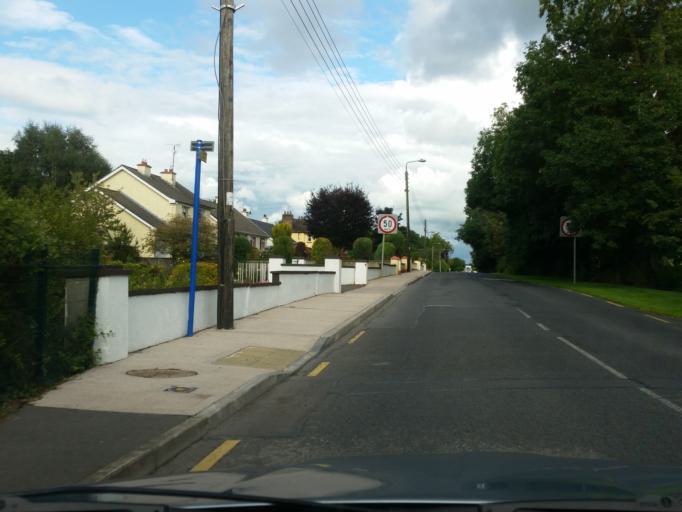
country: IE
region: Ulster
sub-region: County Monaghan
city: Clones
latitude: 54.1787
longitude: -7.2481
